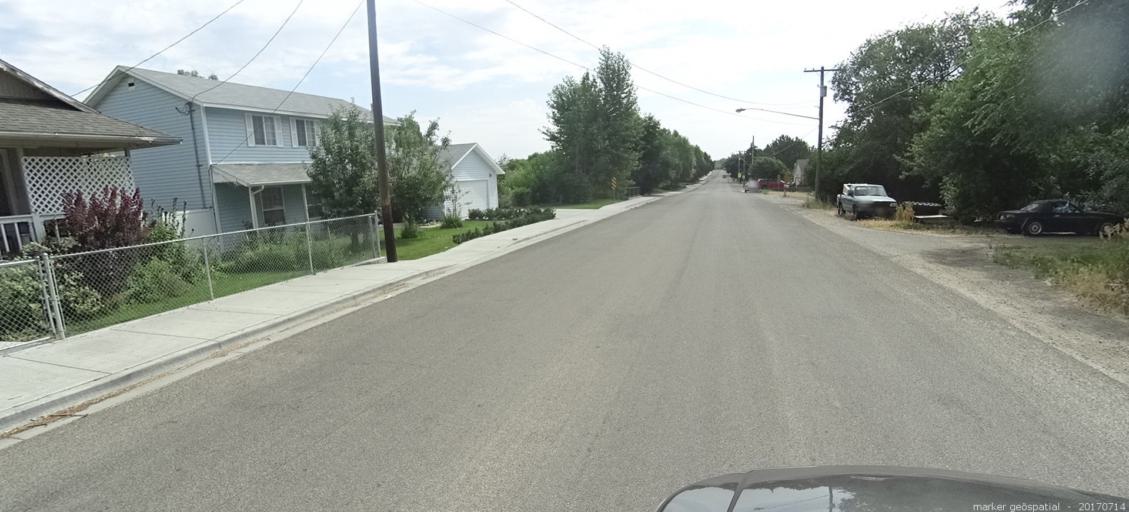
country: US
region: Idaho
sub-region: Ada County
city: Kuna
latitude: 43.4921
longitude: -116.4122
